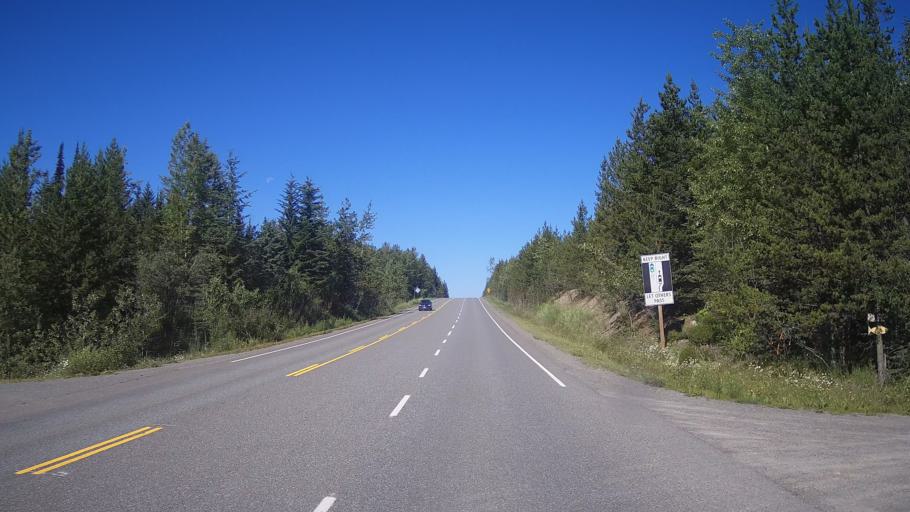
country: CA
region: British Columbia
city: Kamloops
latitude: 51.4977
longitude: -120.3707
